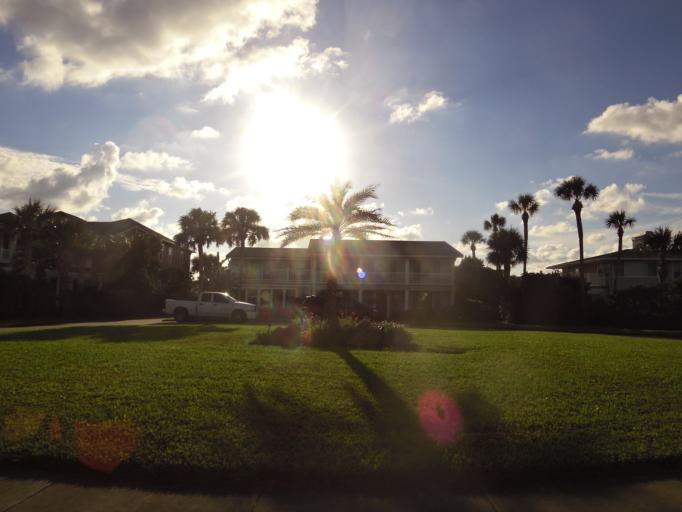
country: US
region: Florida
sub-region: Saint Johns County
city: Ponte Vedra Beach
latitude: 30.2226
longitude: -81.3733
